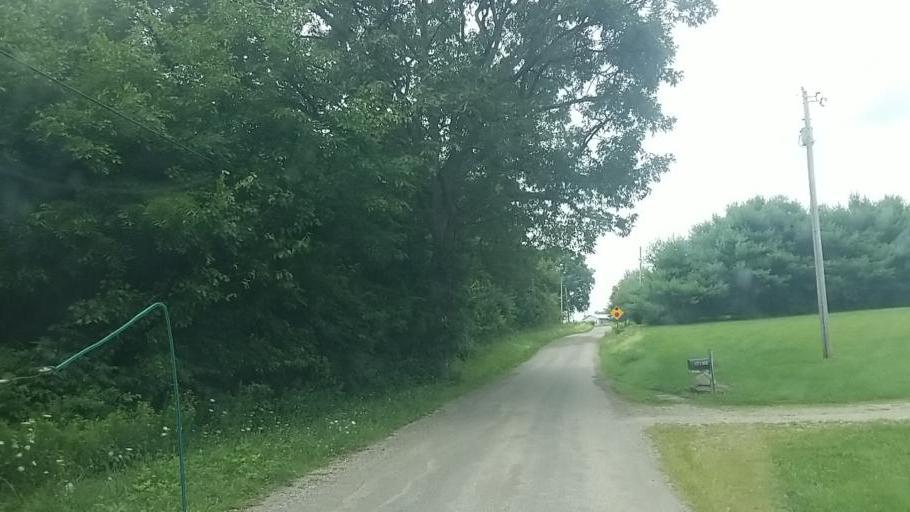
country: US
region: Ohio
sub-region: Licking County
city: Utica
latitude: 40.1973
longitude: -82.3342
